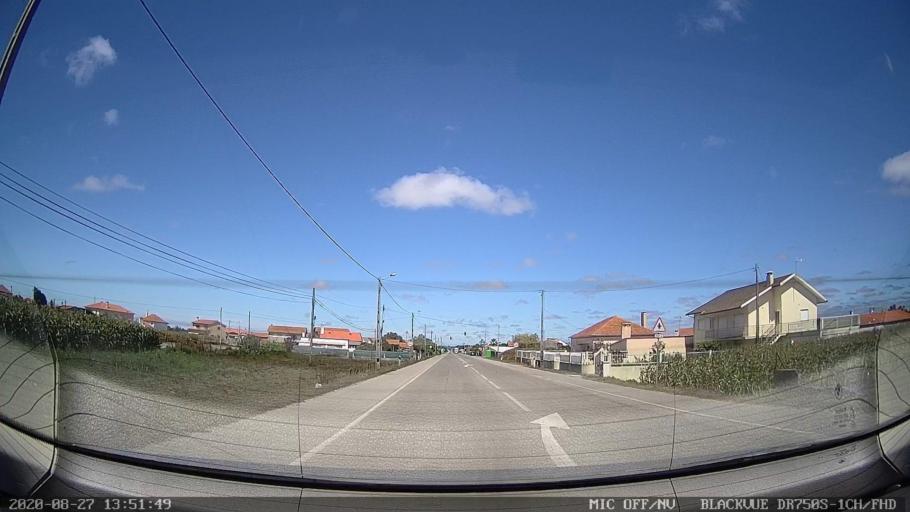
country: PT
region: Coimbra
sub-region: Mira
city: Mira
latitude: 40.3444
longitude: -8.7494
